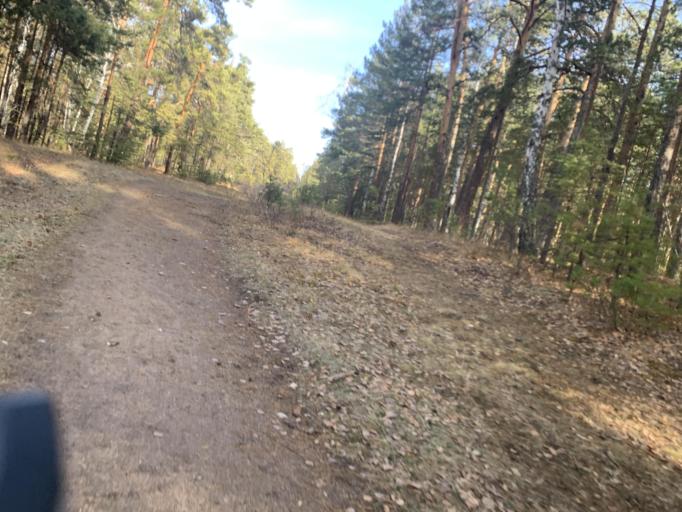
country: RU
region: Chelyabinsk
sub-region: Gorod Chelyabinsk
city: Chelyabinsk
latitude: 55.1542
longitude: 61.3504
